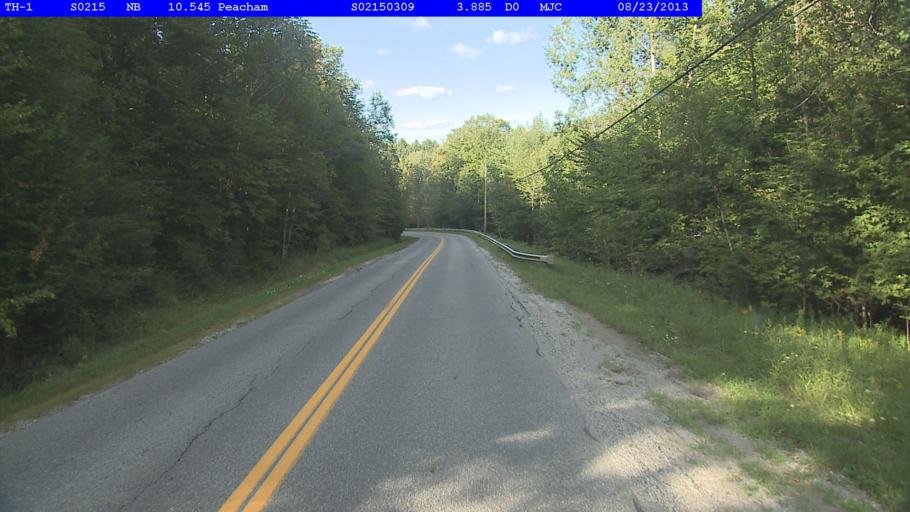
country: US
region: Vermont
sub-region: Caledonia County
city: Saint Johnsbury
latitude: 44.3523
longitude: -72.1773
